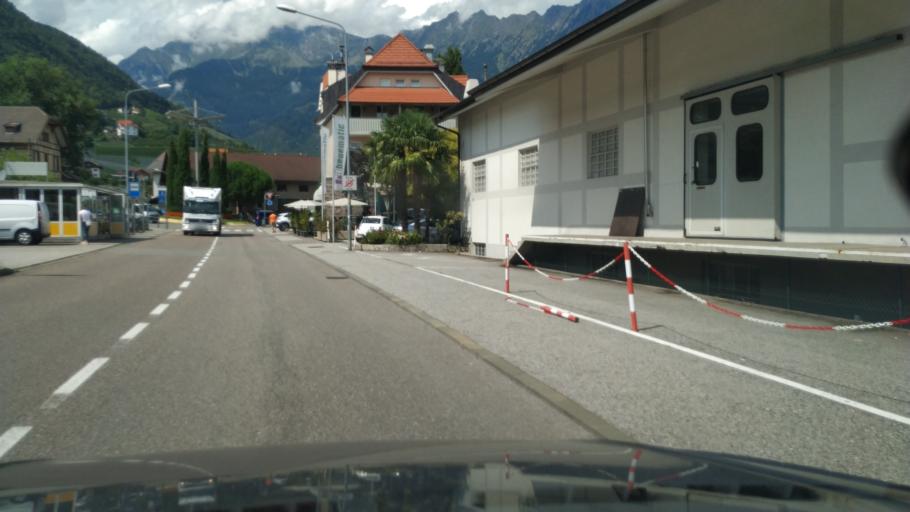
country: IT
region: Trentino-Alto Adige
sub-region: Bolzano
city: Marlengo
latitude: 46.6560
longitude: 11.1494
